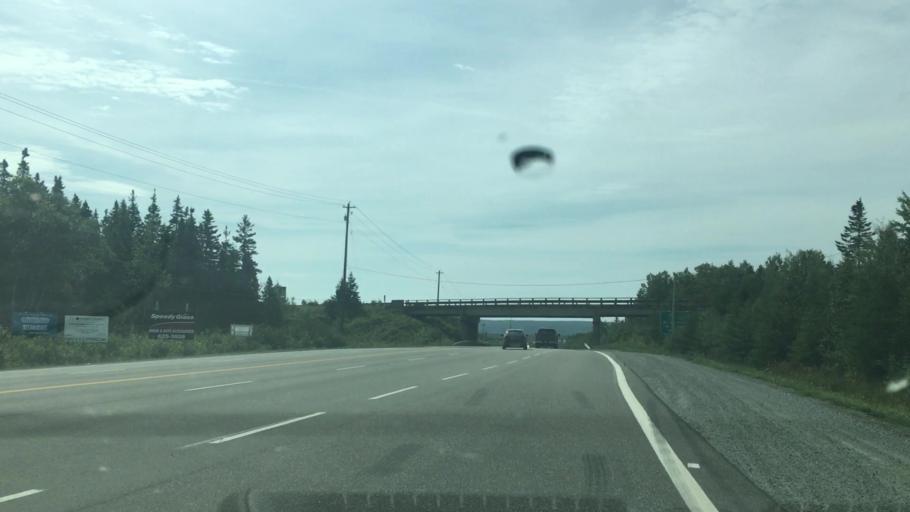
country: CA
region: Nova Scotia
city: Port Hawkesbury
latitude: 45.6262
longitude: -61.3322
